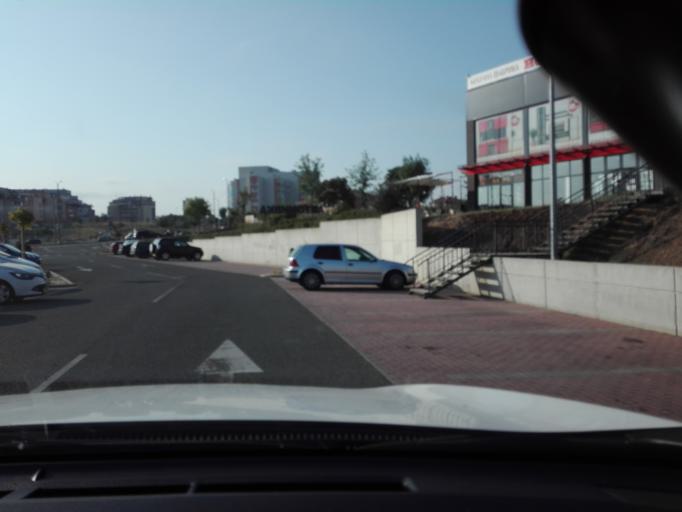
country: BG
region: Burgas
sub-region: Obshtina Burgas
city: Burgas
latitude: 42.4633
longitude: 27.4094
